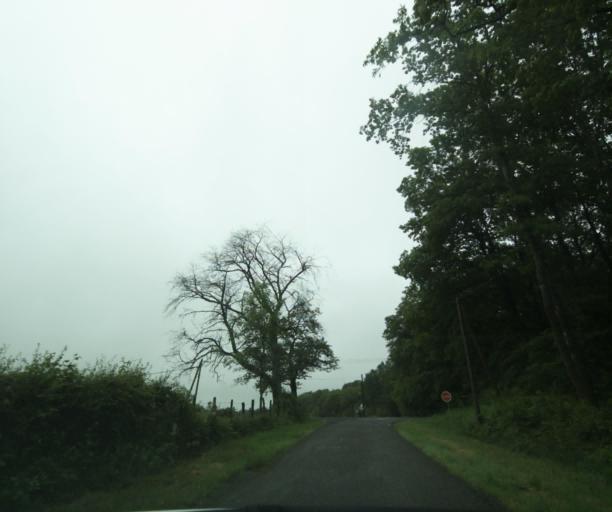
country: FR
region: Bourgogne
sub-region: Departement de Saone-et-Loire
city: Charolles
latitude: 46.4607
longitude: 4.2501
